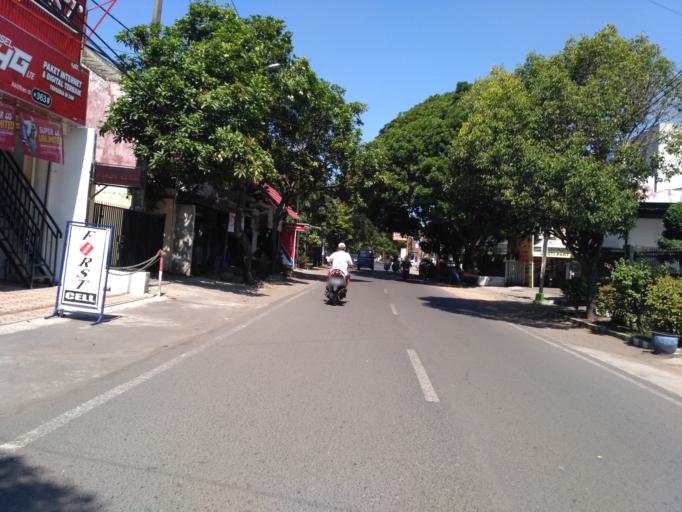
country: ID
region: East Java
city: Malang
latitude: -7.9735
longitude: 112.6665
